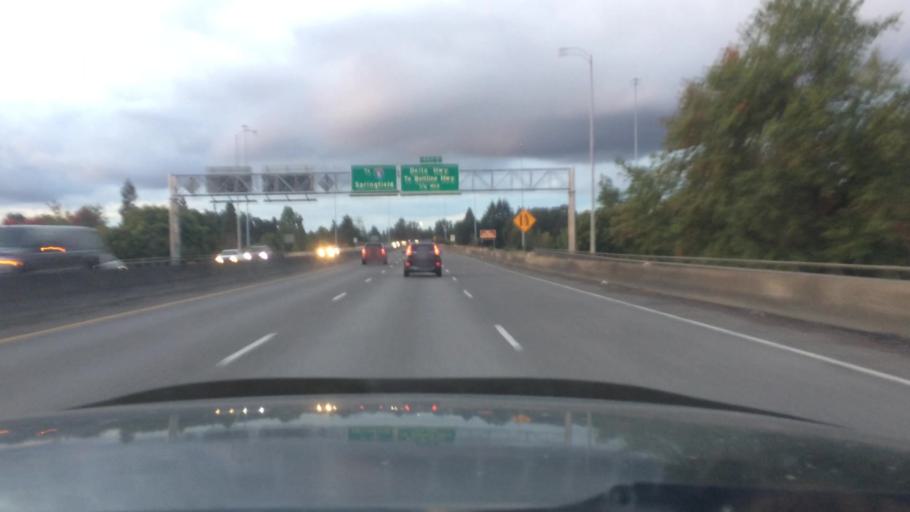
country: US
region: Oregon
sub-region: Lane County
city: Eugene
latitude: 44.0578
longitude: -123.1010
